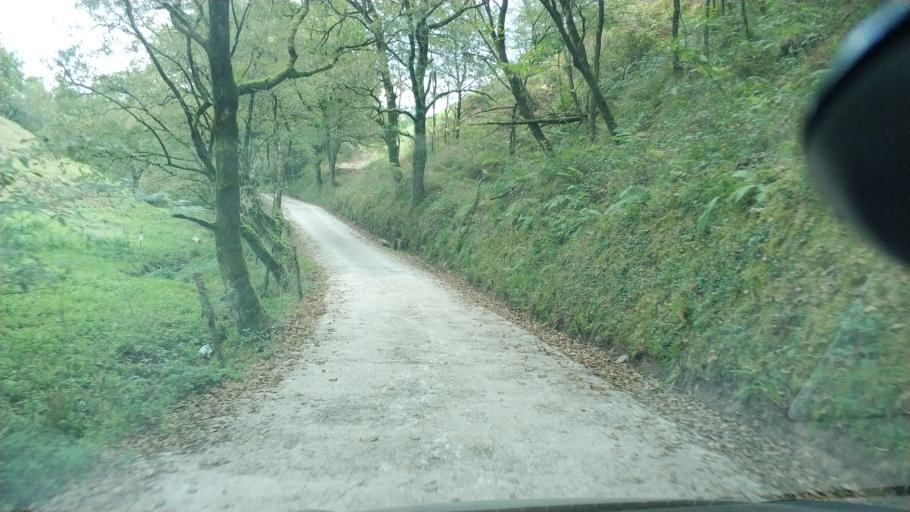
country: ES
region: Cantabria
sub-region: Provincia de Cantabria
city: Santa Maria de Cayon
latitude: 43.2945
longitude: -3.8558
